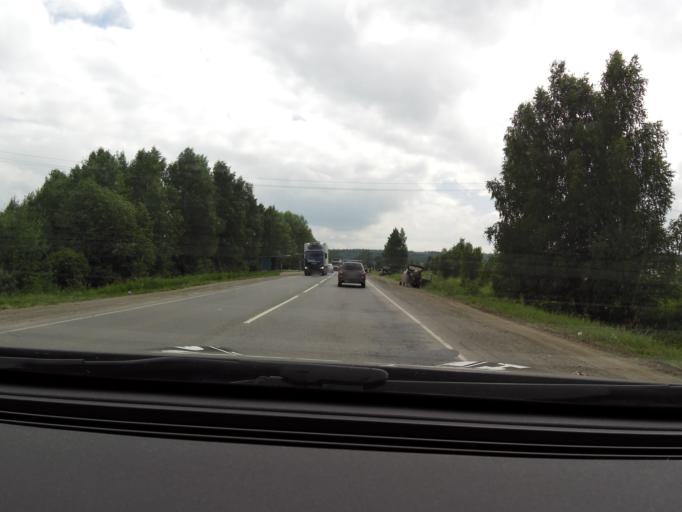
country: RU
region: Perm
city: Kukushtan
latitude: 57.4945
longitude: 56.6610
